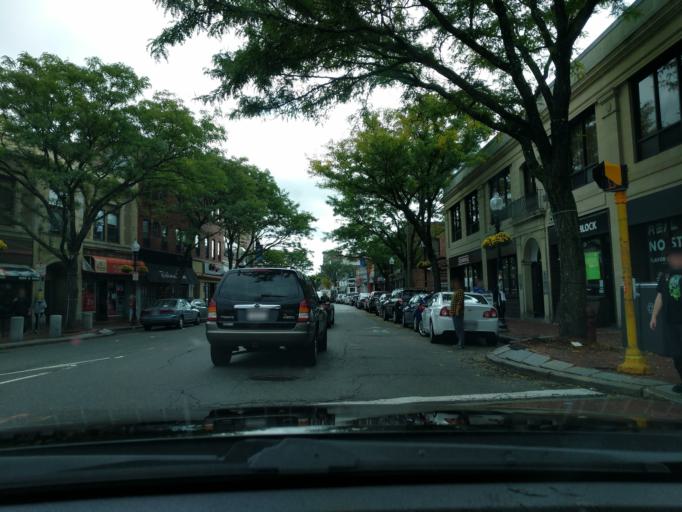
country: US
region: Massachusetts
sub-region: Middlesex County
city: Somerville
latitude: 42.3963
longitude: -71.1224
